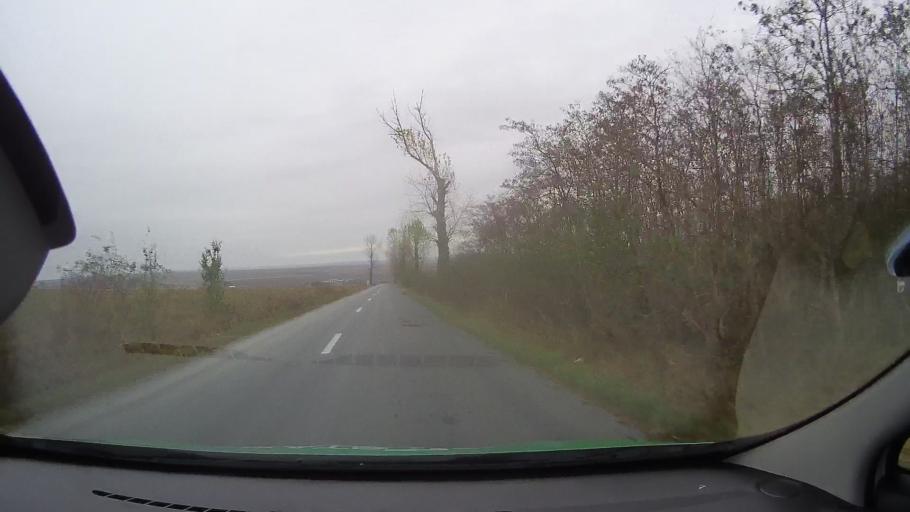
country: RO
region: Constanta
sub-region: Comuna Pantelimon
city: Pantelimon
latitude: 44.5857
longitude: 28.3139
